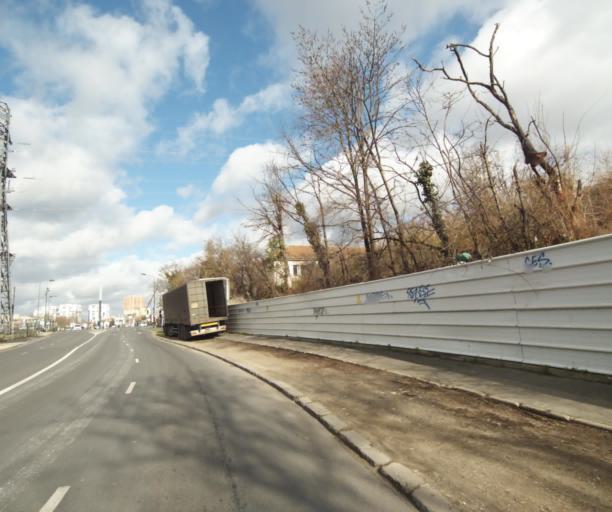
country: FR
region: Ile-de-France
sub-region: Departement de Seine-Saint-Denis
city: Villetaneuse
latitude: 48.9461
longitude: 2.3431
